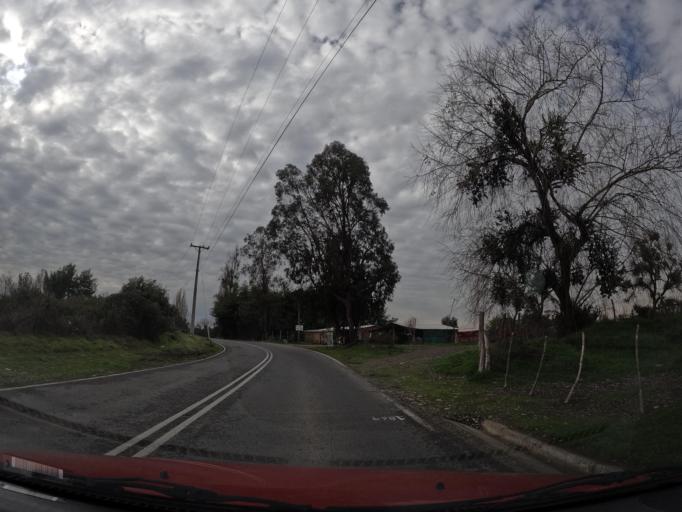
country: CL
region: Maule
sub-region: Provincia de Linares
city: Linares
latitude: -35.8631
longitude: -71.6178
